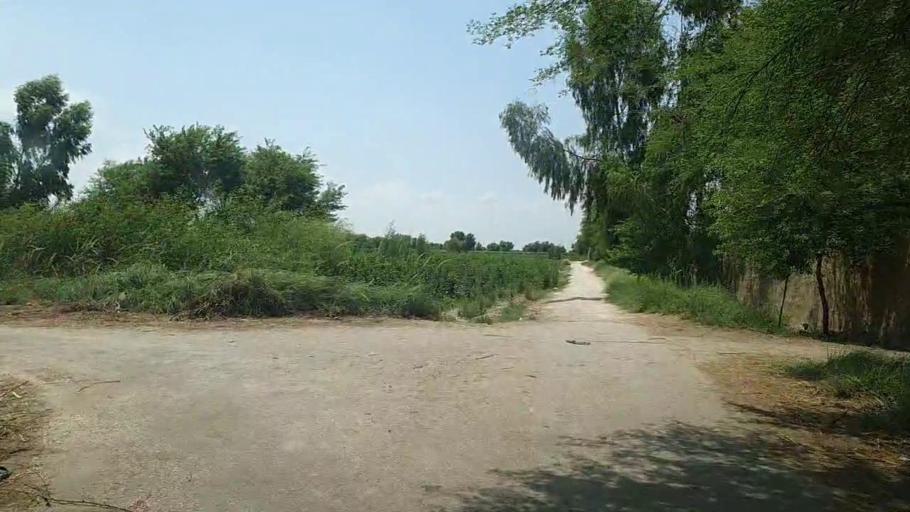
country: PK
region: Sindh
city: Ubauro
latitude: 28.1513
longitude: 69.7689
